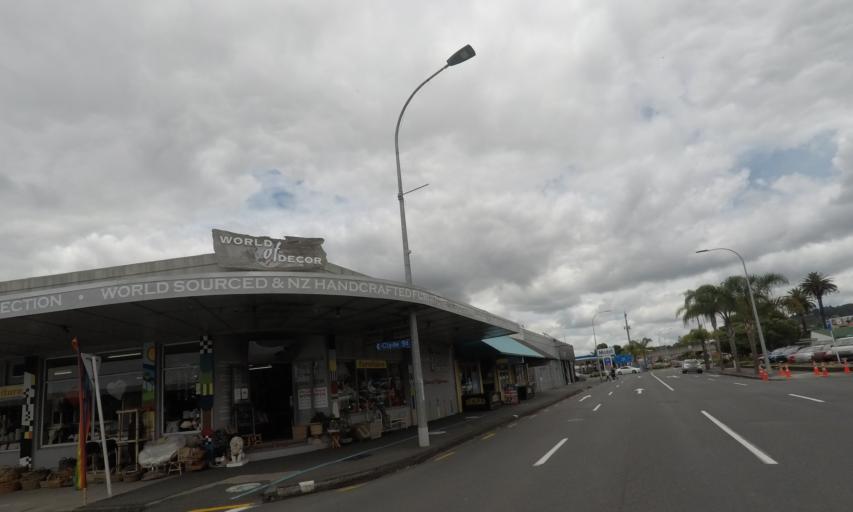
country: NZ
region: Northland
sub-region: Whangarei
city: Whangarei
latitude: -35.7269
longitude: 174.3213
